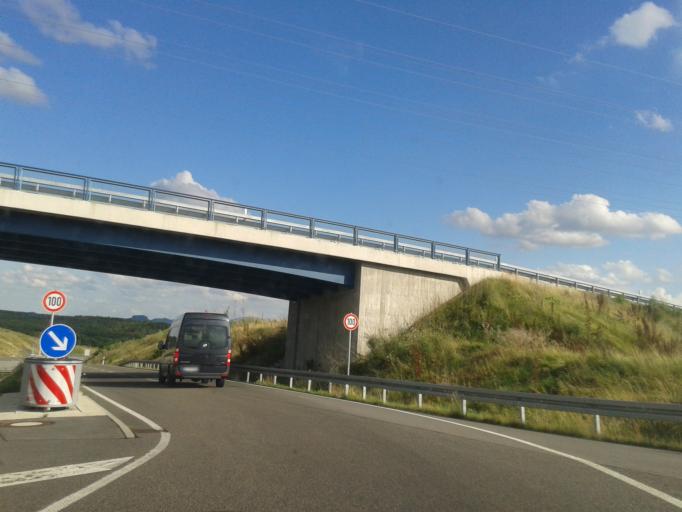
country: DE
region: Saxony
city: Durrrohrsdorf
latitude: 51.0115
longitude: 13.9541
